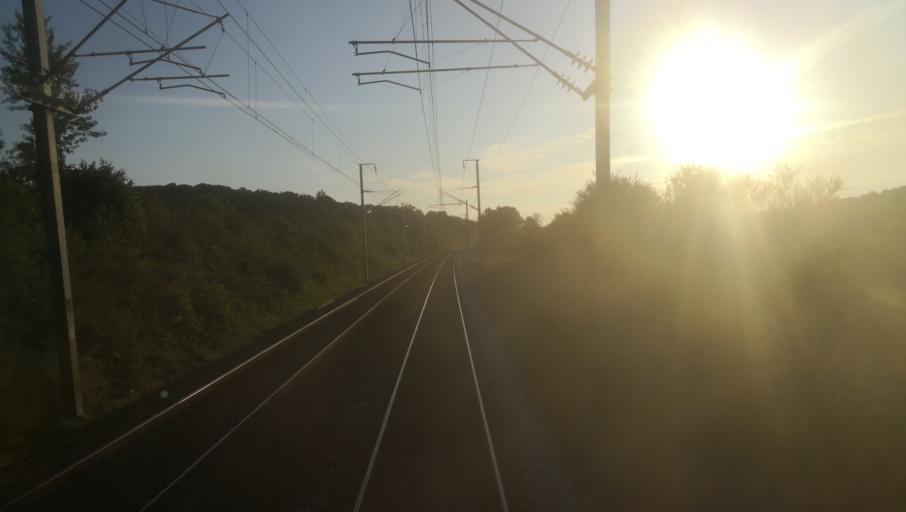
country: FR
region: Lower Normandy
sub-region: Departement du Calvados
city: La Vespiere
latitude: 49.0755
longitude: 0.3987
